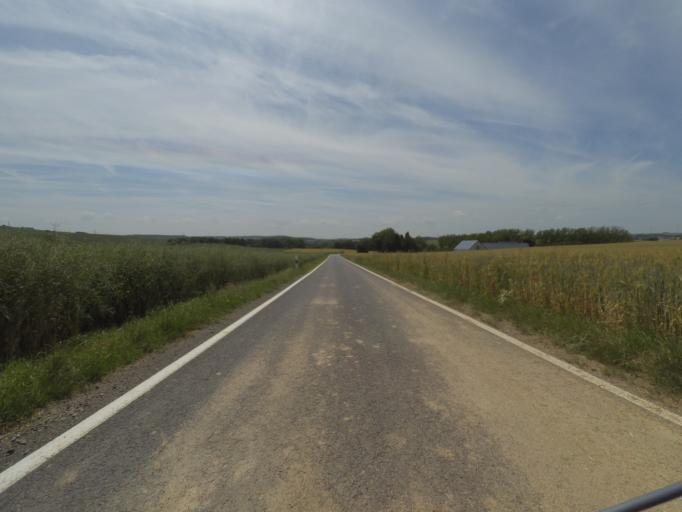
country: DE
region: Rheinland-Pfalz
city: Wierschem
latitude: 50.2351
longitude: 7.3378
